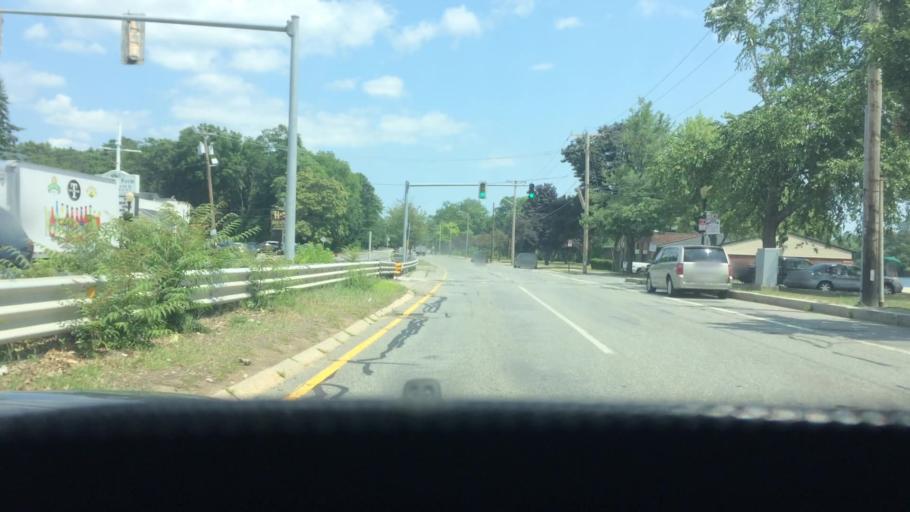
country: US
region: Massachusetts
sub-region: Middlesex County
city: Lowell
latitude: 42.6431
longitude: -71.3408
